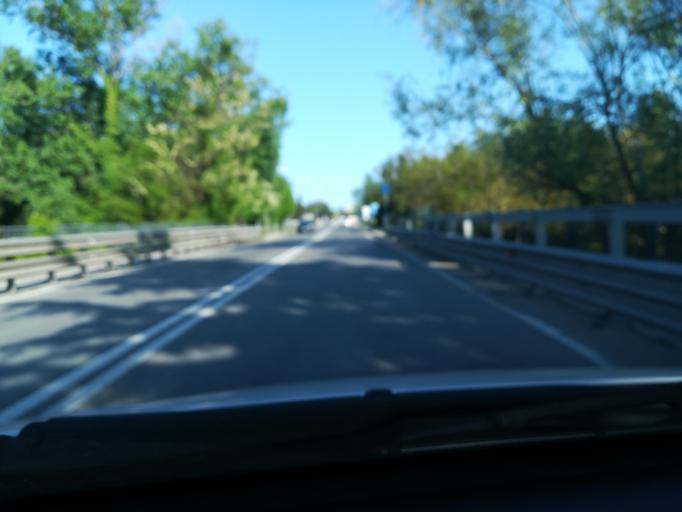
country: IT
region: Emilia-Romagna
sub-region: Provincia di Rimini
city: Riccione
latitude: 44.0003
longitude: 12.6425
